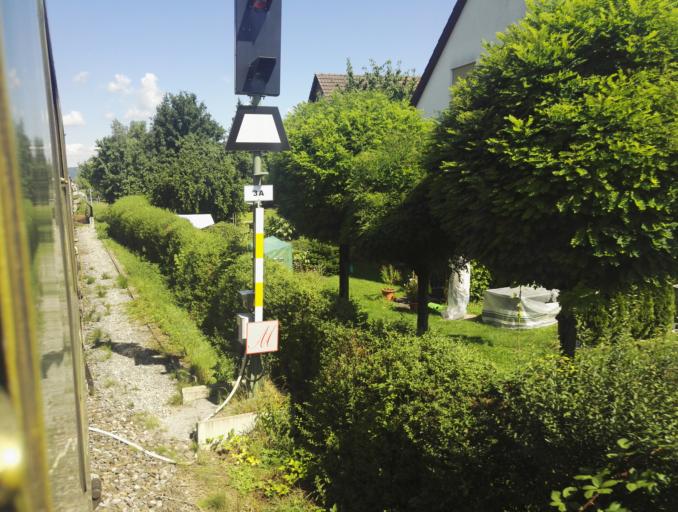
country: DE
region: Baden-Wuerttemberg
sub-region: Regierungsbezirk Stuttgart
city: Schorndorf
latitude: 48.8418
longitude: 9.5400
